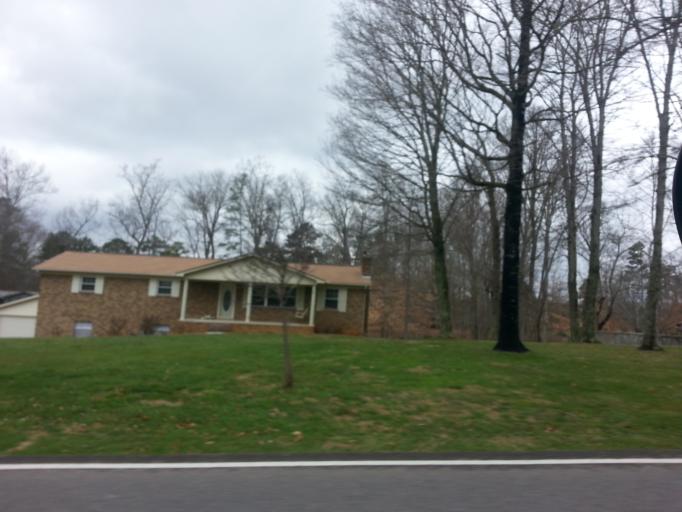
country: US
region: Tennessee
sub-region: Union County
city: Condon
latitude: 36.1103
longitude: -83.8844
